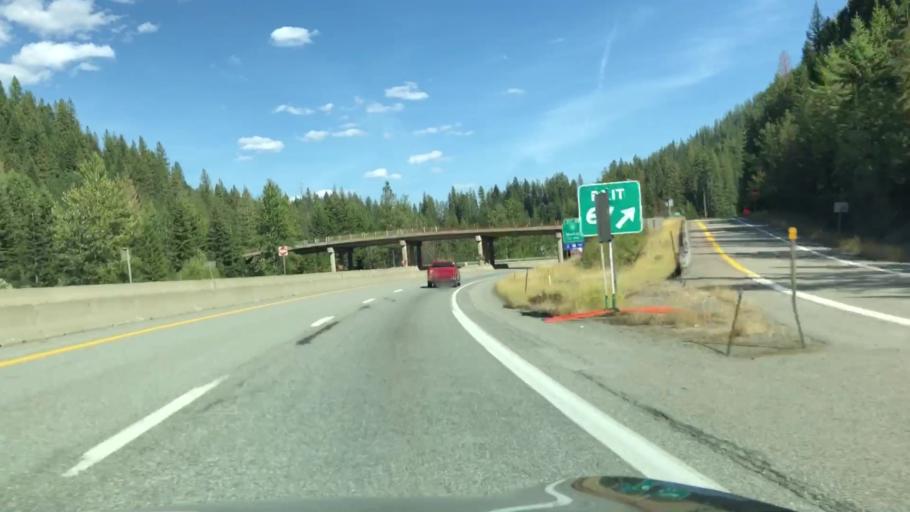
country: US
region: Idaho
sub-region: Shoshone County
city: Wallace
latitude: 47.4657
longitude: -115.8149
